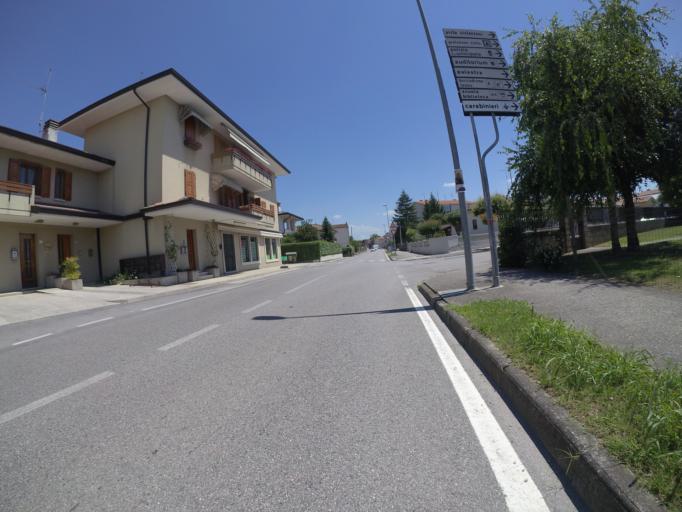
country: IT
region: Friuli Venezia Giulia
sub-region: Provincia di Udine
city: Rivignano
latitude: 45.8782
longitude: 13.0378
